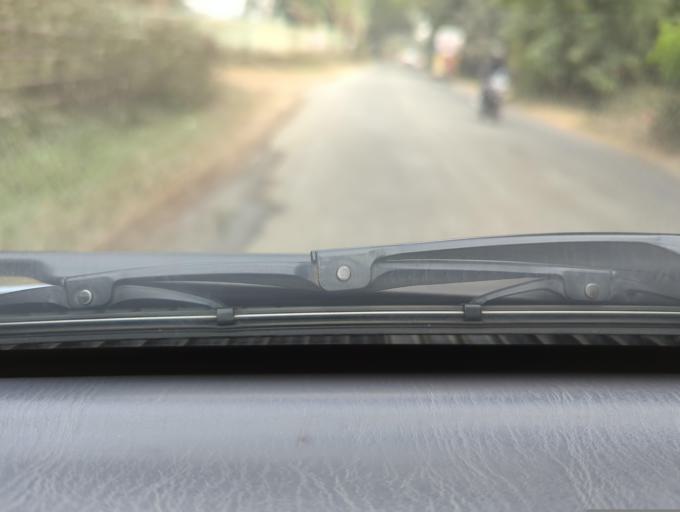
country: BD
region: Sylhet
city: Maulavi Bazar
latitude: 24.5047
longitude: 91.7349
